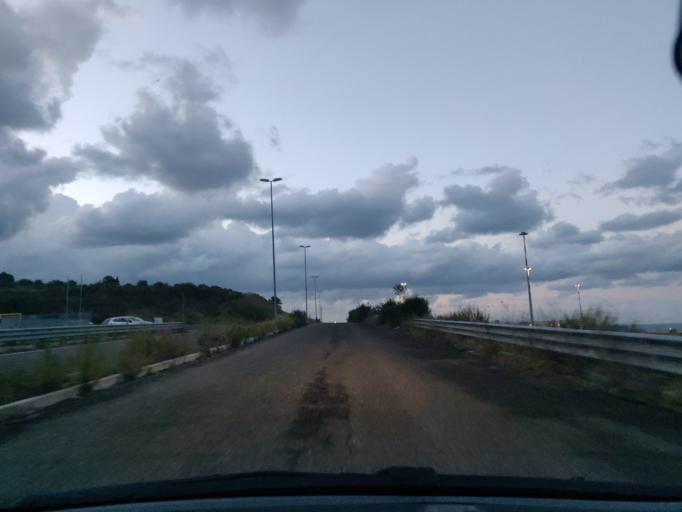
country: IT
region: Latium
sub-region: Citta metropolitana di Roma Capitale
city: Aurelia
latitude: 42.1276
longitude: 11.7781
